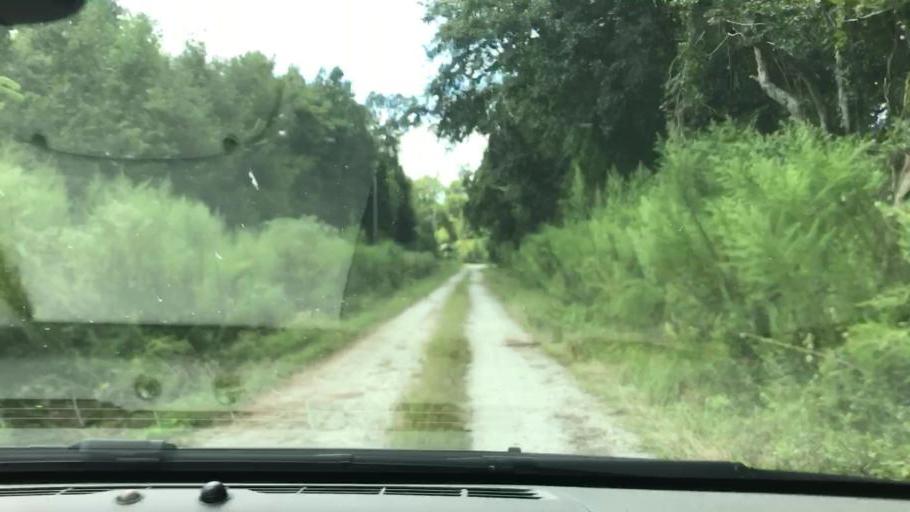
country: US
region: Georgia
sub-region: Quitman County
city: Georgetown
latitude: 31.9947
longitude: -85.0488
